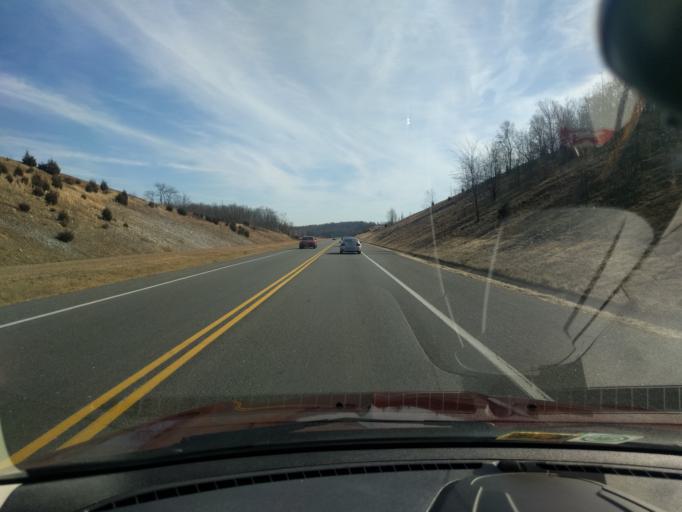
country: US
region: Virginia
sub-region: City of Staunton
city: Staunton
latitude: 38.1395
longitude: -79.1078
